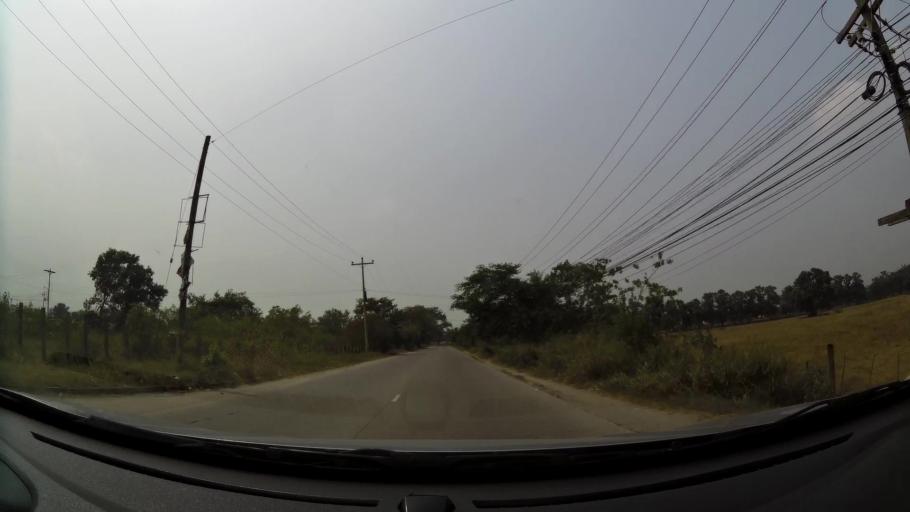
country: HN
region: Cortes
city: La Lima
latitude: 15.4343
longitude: -87.9035
